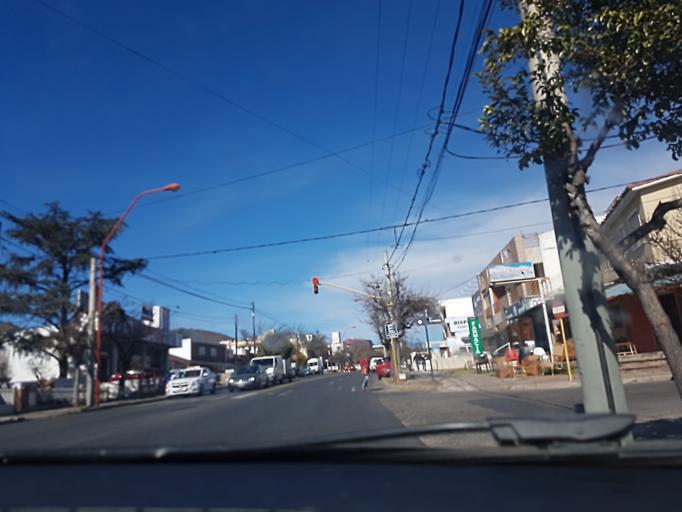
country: AR
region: Cordoba
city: Villa Carlos Paz
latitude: -31.4258
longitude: -64.4953
